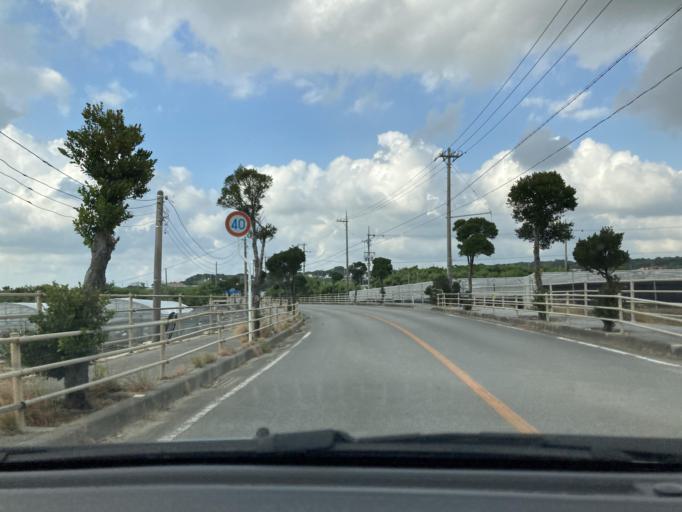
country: JP
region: Okinawa
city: Itoman
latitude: 26.0988
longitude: 127.6657
